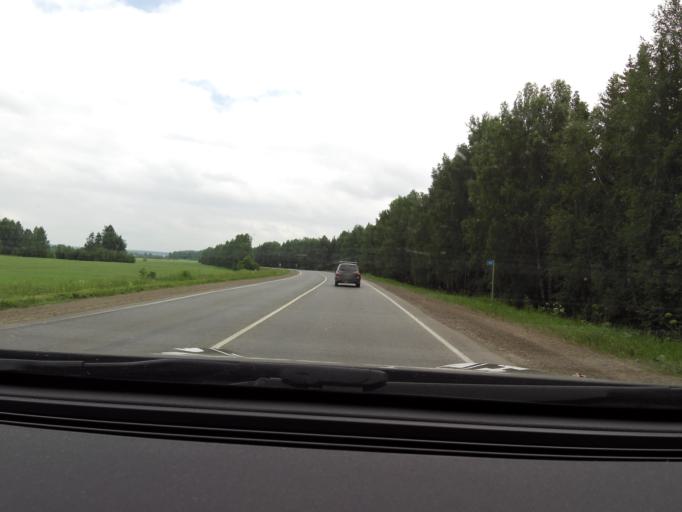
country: RU
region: Perm
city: Kukushtan
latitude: 57.4836
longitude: 56.6768
